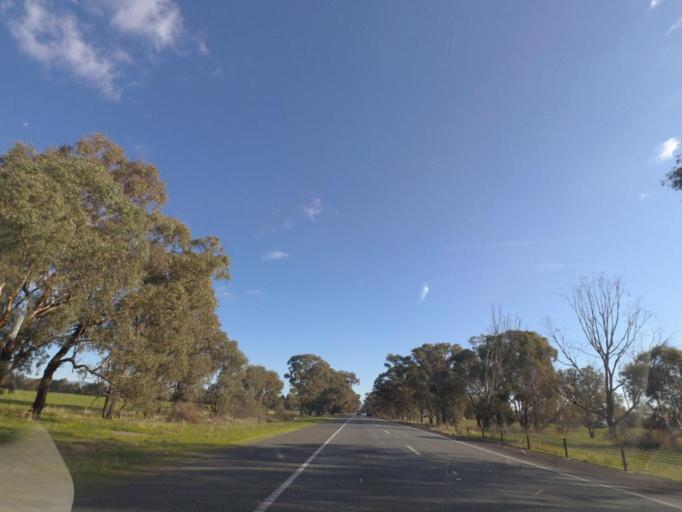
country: AU
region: Victoria
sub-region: Benalla
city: Benalla
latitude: -36.6910
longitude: 145.6622
